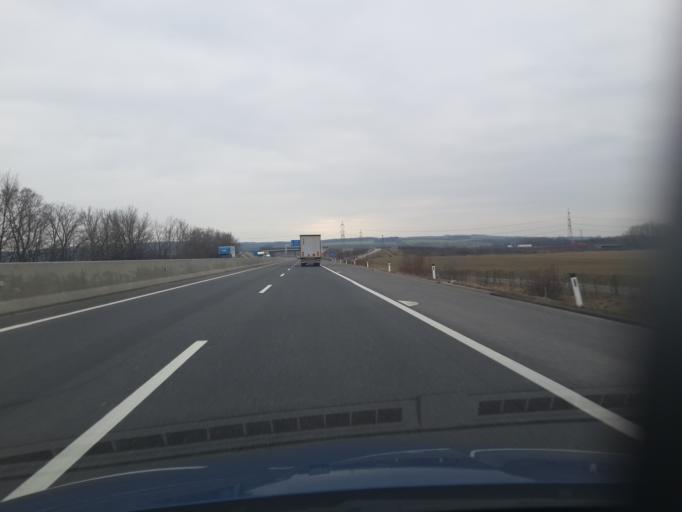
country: AT
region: Burgenland
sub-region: Politischer Bezirk Neusiedl am See
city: Parndorf
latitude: 48.0244
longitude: 16.8466
